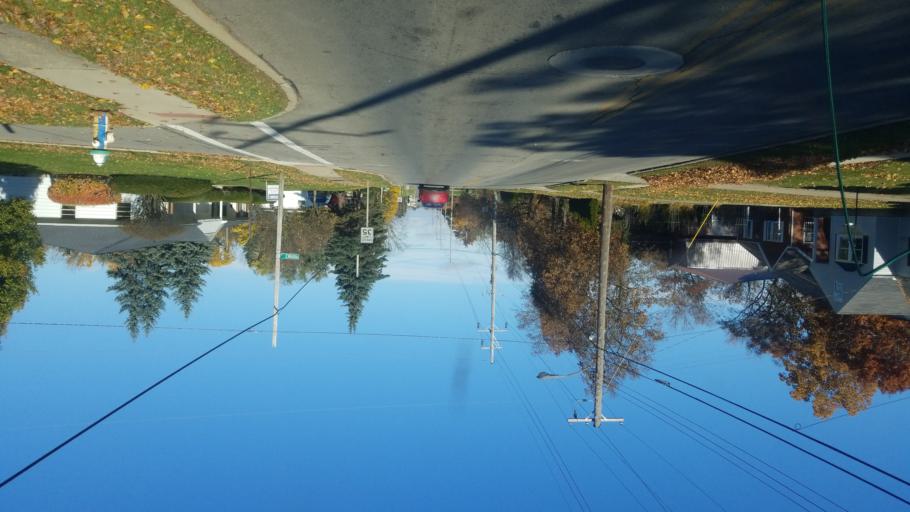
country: US
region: Ohio
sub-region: Richland County
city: Mansfield
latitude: 40.7547
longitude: -82.5517
